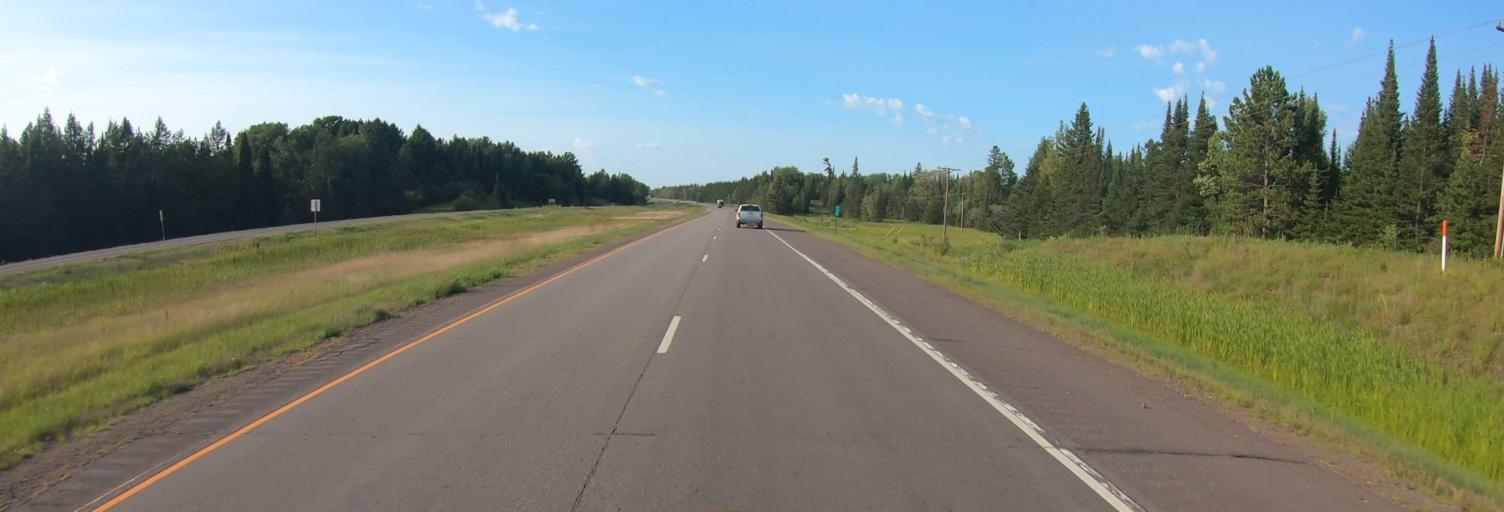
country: US
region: Minnesota
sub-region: Saint Louis County
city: Eveleth
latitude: 47.1261
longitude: -92.4721
